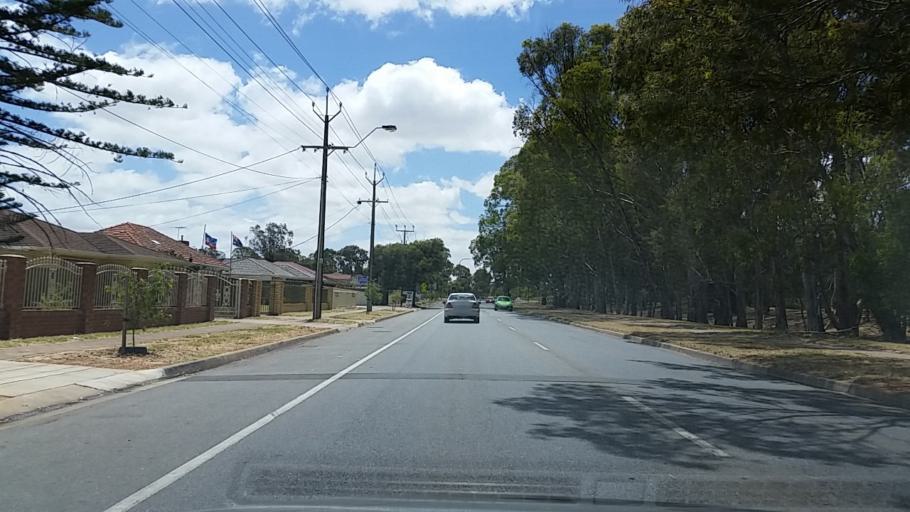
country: AU
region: South Australia
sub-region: Salisbury
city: Salisbury
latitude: -34.7701
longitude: 138.6186
